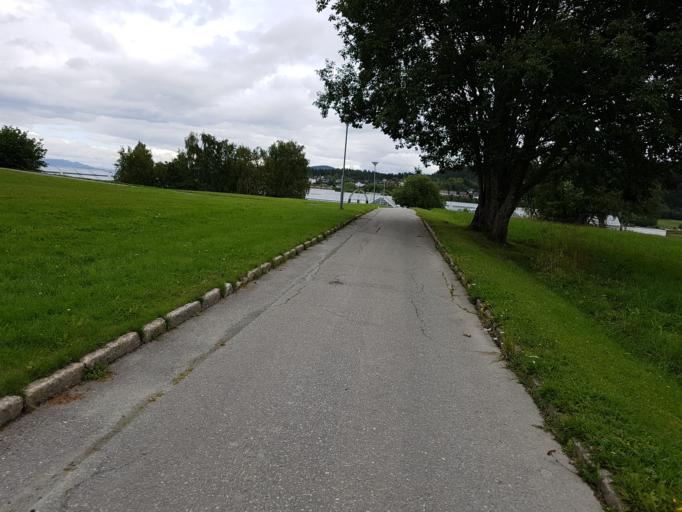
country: NO
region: Sor-Trondelag
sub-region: Trondheim
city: Trondheim
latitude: 63.4078
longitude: 10.4658
